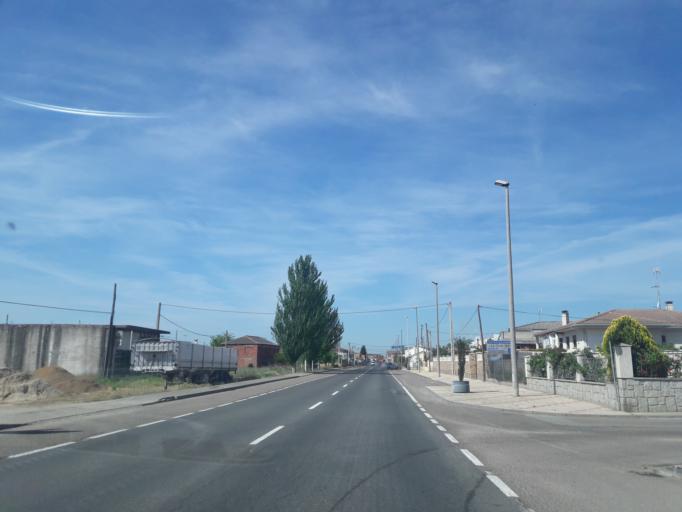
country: ES
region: Castille and Leon
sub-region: Provincia de Salamanca
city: Babilafuente
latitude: 40.9769
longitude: -5.4219
